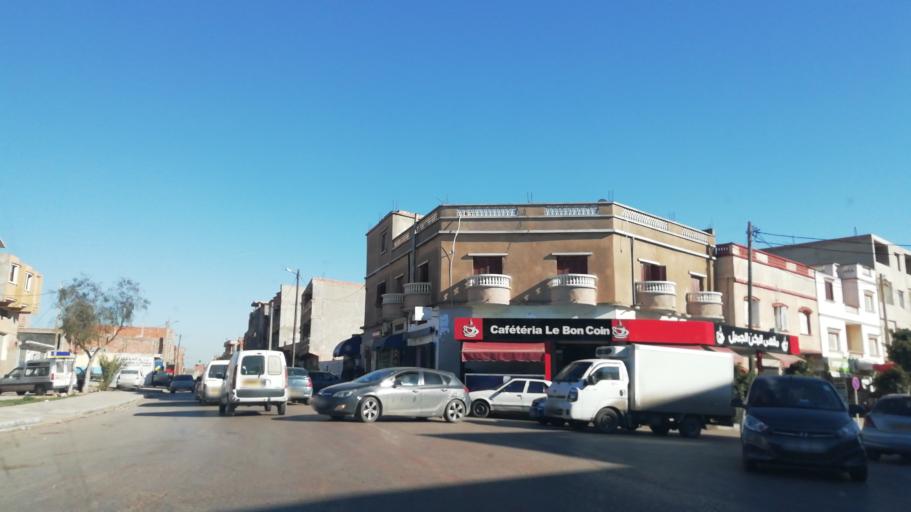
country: DZ
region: Oran
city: Bir el Djir
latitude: 35.7261
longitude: -0.5450
